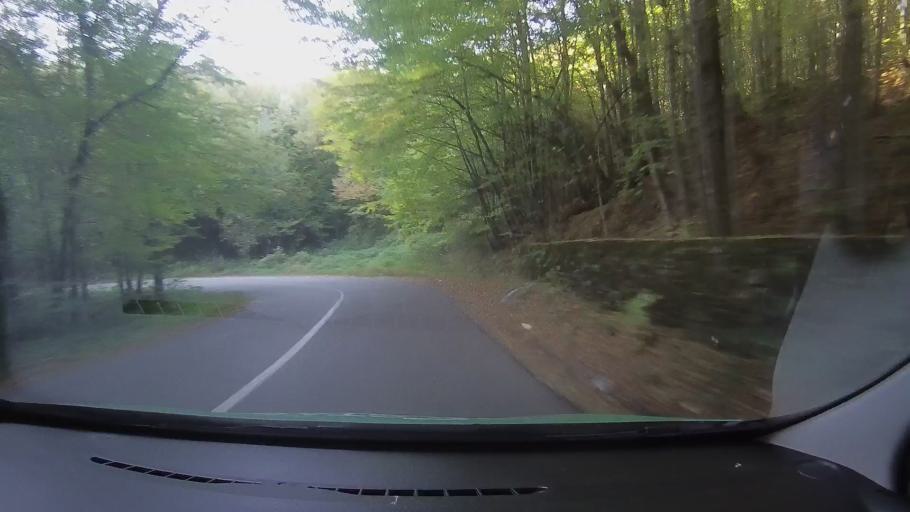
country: RO
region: Timis
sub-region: Comuna Nadrag
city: Nadrag
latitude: 45.6761
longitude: 22.1667
